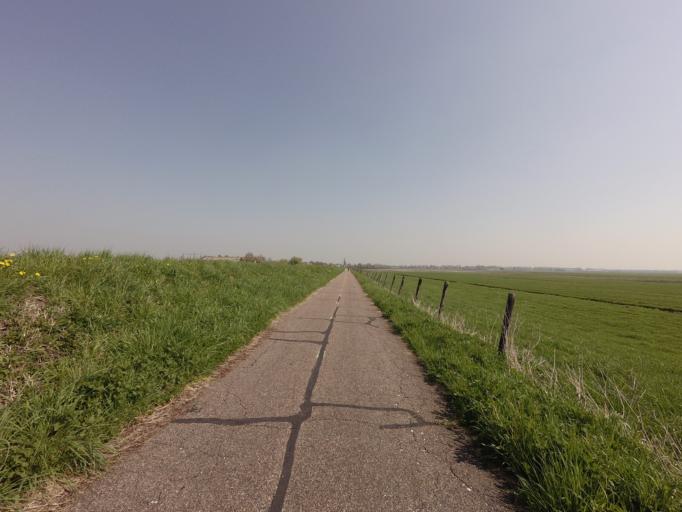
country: NL
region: Utrecht
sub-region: Gemeente De Ronde Venen
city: Mijdrecht
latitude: 52.1912
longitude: 4.8602
